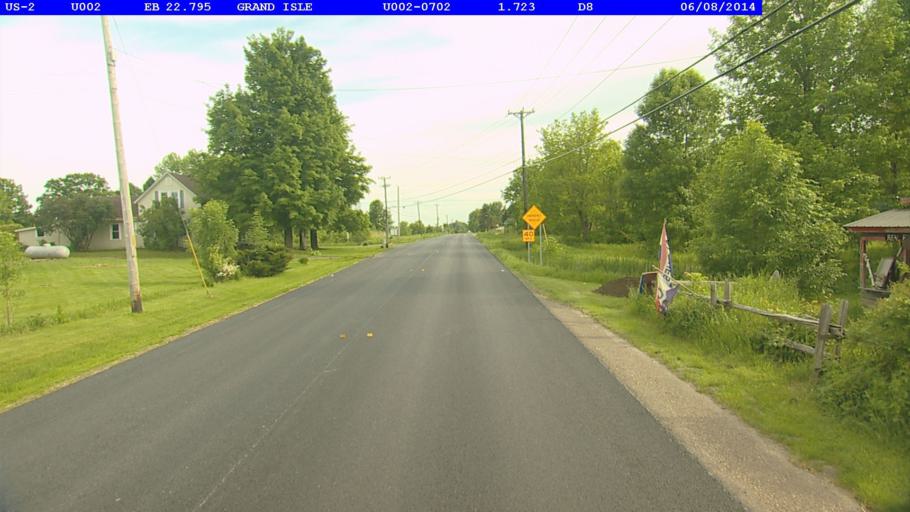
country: US
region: Vermont
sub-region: Grand Isle County
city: North Hero
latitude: 44.7426
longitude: -73.2892
